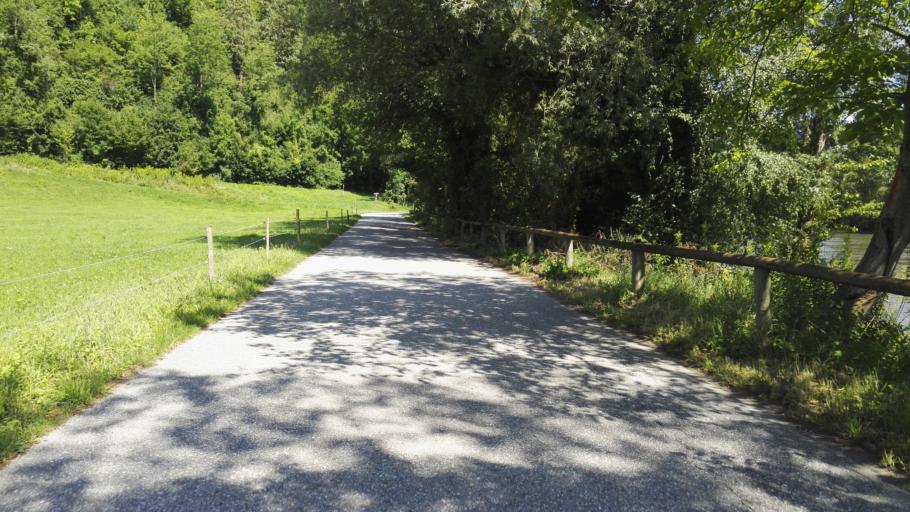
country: AT
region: Styria
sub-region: Politischer Bezirk Graz-Umgebung
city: Frohnleiten
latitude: 47.2455
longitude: 15.3107
